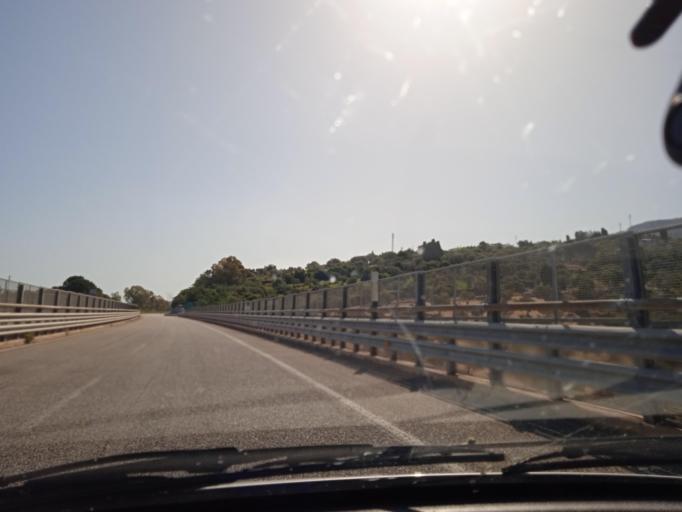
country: IT
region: Sicily
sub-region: Messina
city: Acquedolci
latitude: 38.0477
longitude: 14.5634
